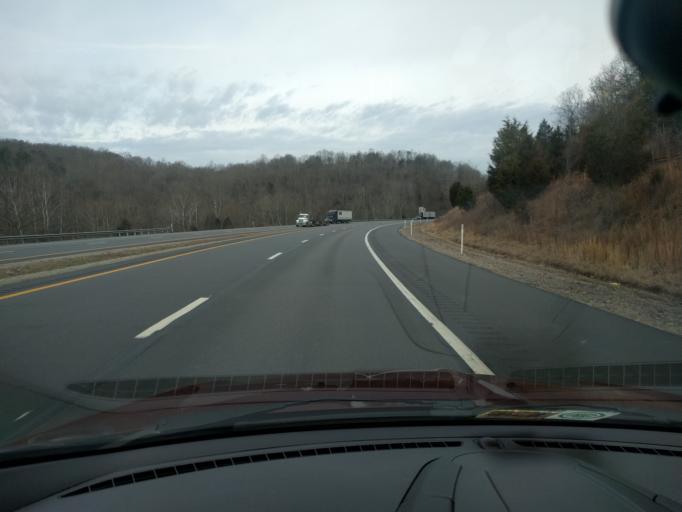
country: US
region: West Virginia
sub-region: Jackson County
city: Ripley
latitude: 38.7675
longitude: -81.7167
